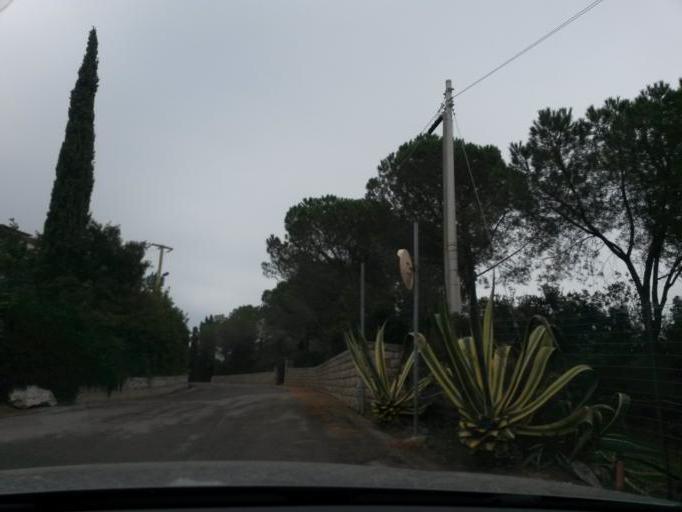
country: IT
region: Tuscany
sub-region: Provincia di Livorno
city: Capoliveri
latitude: 42.7499
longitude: 10.3622
